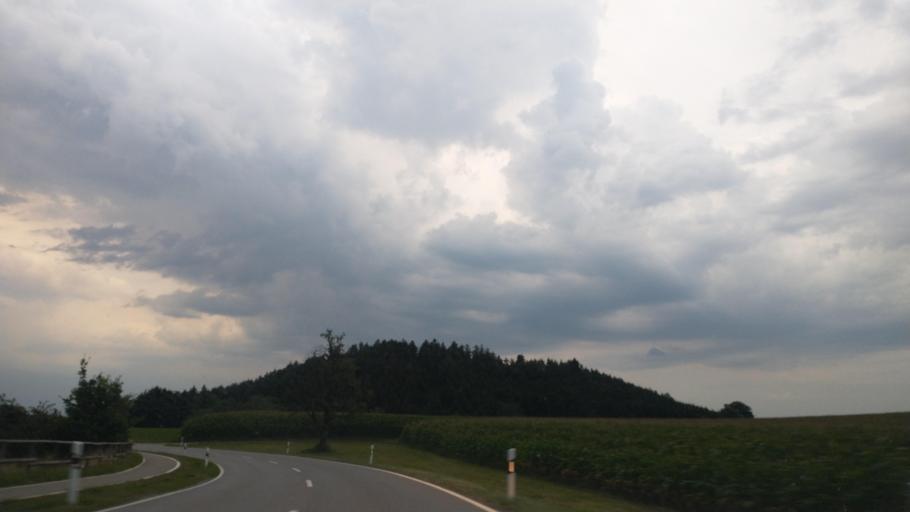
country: DE
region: Baden-Wuerttemberg
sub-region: Tuebingen Region
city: Neukirch
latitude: 47.6649
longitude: 9.7206
